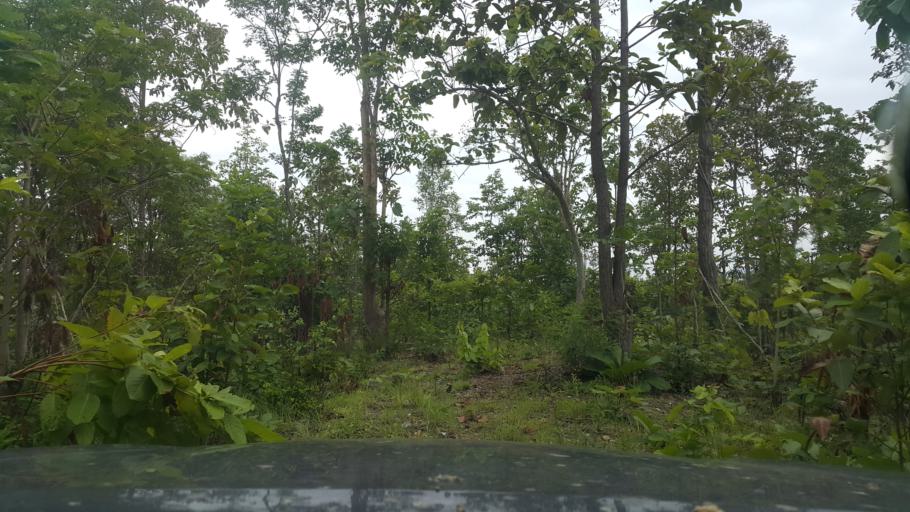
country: TH
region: Chiang Mai
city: Hang Dong
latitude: 18.6926
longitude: 98.8600
